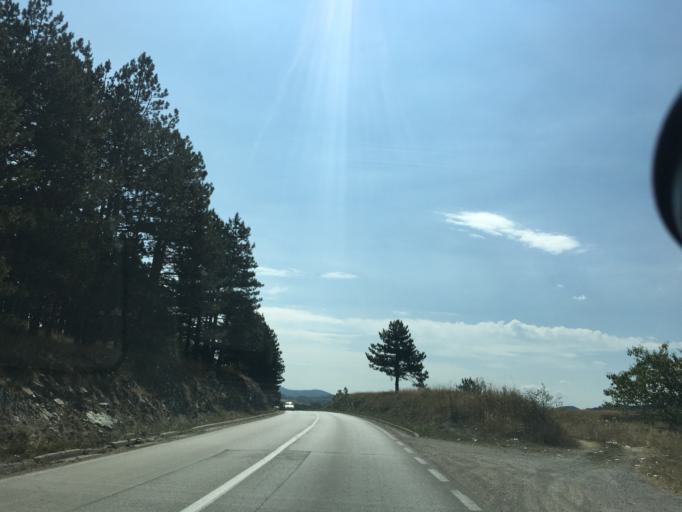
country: RS
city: Zlatibor
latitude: 43.6914
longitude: 19.6945
